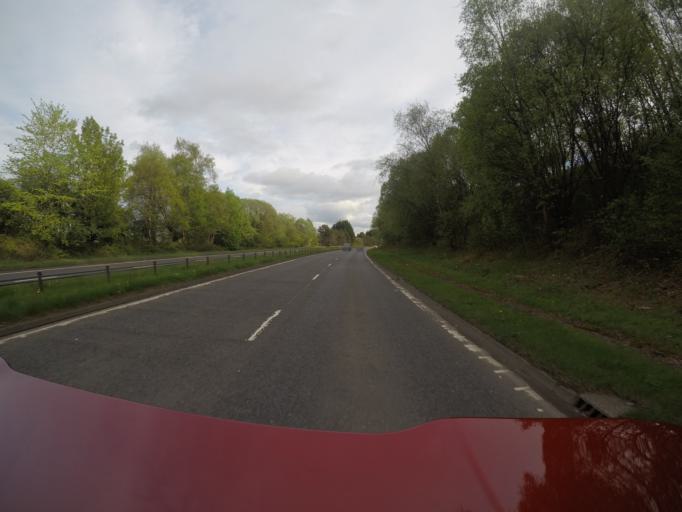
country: GB
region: Scotland
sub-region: West Dunbartonshire
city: Alexandria
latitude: 55.9880
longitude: -4.5893
